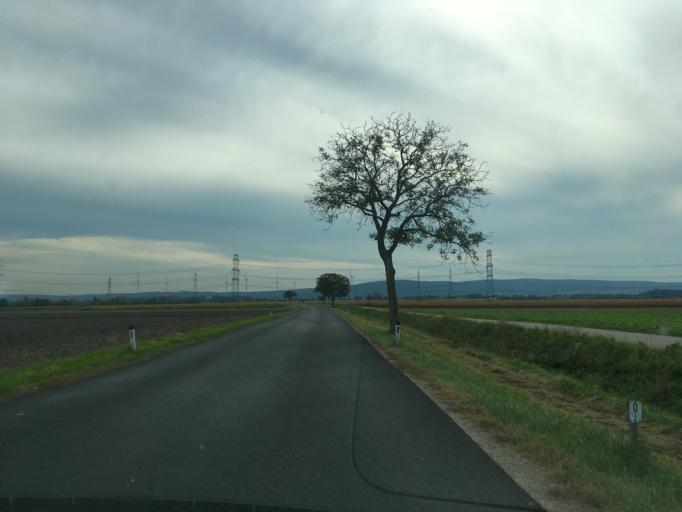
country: AT
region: Lower Austria
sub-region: Politischer Bezirk Bruck an der Leitha
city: Trautmannsdorf an der Leitha
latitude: 48.0363
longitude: 16.6772
